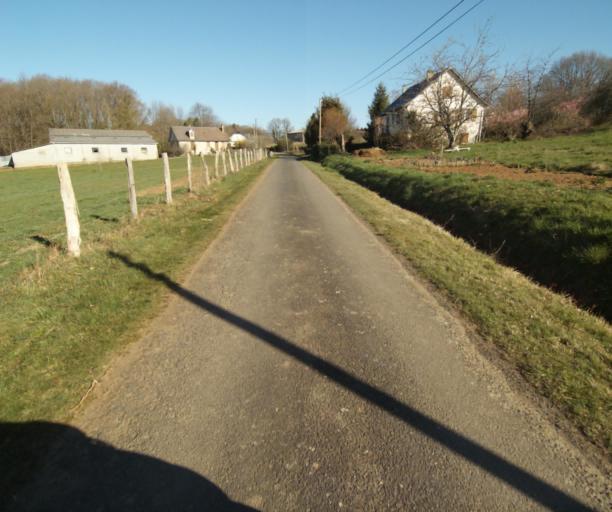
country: FR
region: Limousin
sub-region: Departement de la Correze
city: Saint-Clement
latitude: 45.3821
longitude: 1.6531
